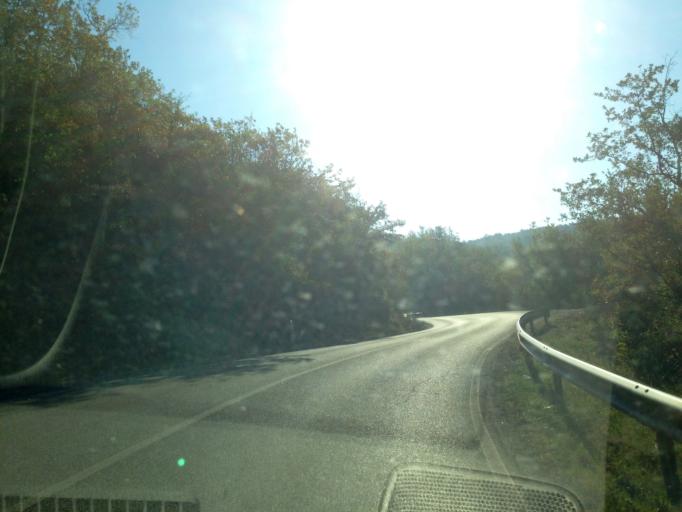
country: IT
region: Tuscany
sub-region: Provincia di Siena
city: Castellina in Chianti
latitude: 43.5033
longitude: 11.2983
